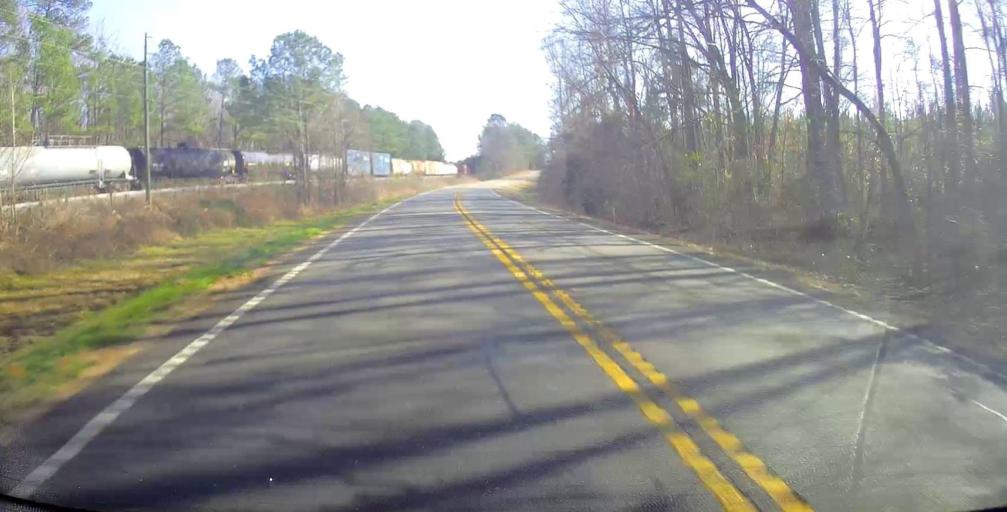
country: US
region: Georgia
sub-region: Talbot County
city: Talbotton
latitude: 32.7366
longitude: -84.5544
